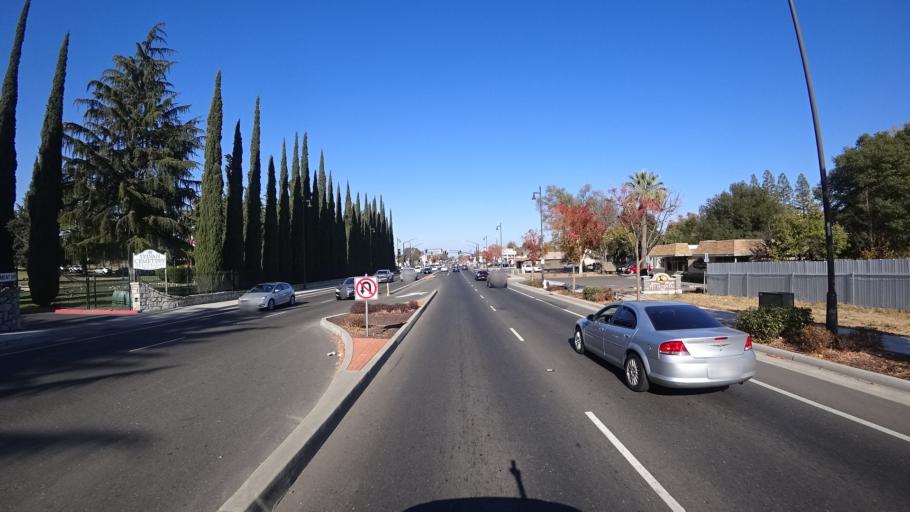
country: US
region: California
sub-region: Sacramento County
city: Citrus Heights
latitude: 38.7000
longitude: -121.2903
